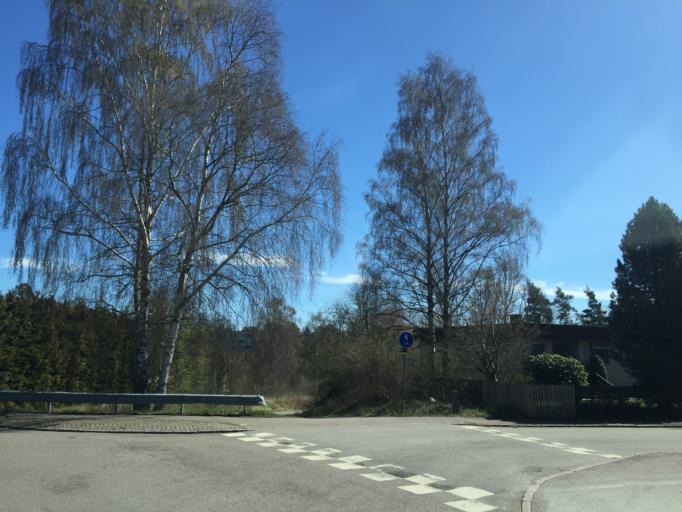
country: SE
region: Kalmar
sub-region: Oskarshamns Kommun
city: Oskarshamn
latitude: 57.2566
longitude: 16.4505
